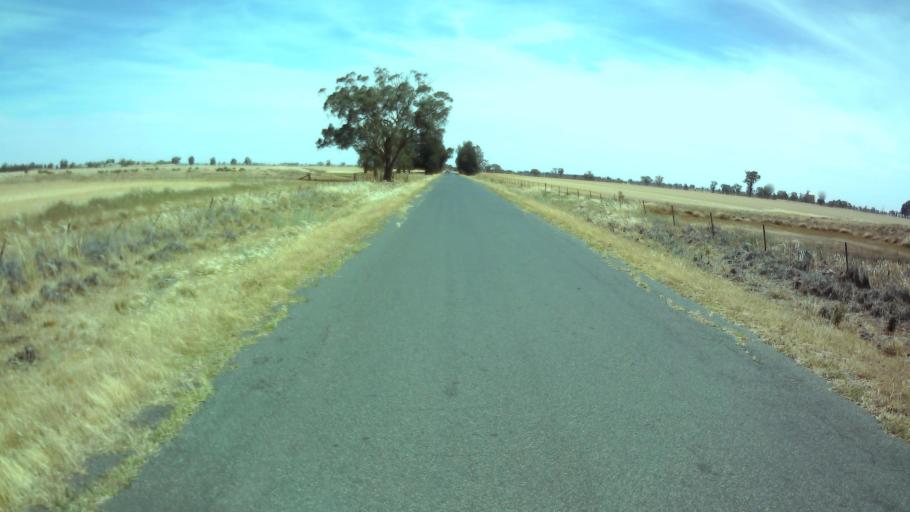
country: AU
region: New South Wales
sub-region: Weddin
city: Grenfell
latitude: -33.9266
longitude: 147.7631
